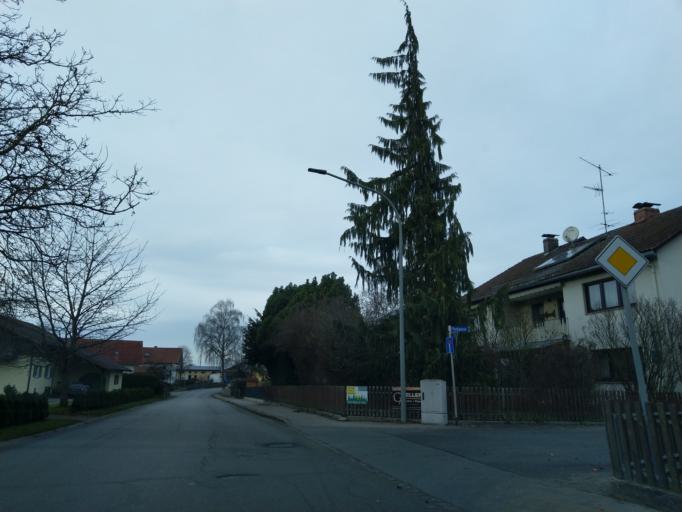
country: DE
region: Bavaria
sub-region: Lower Bavaria
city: Rossbach
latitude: 48.6189
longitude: 12.9821
